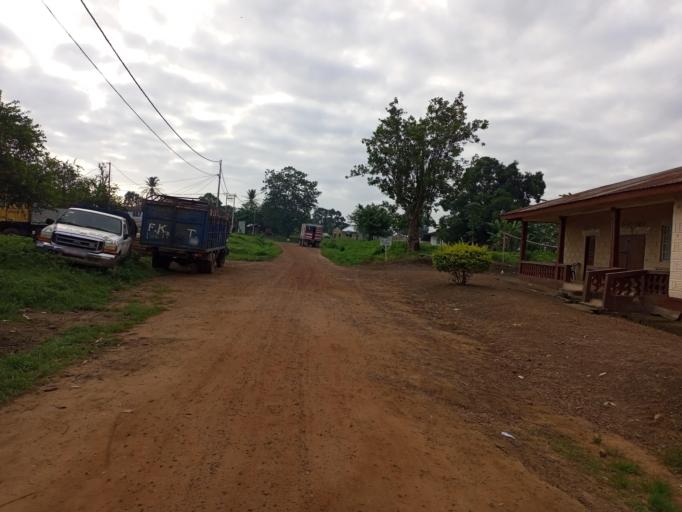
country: SL
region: Eastern Province
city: Pendembu
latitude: 8.0990
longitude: -10.6972
